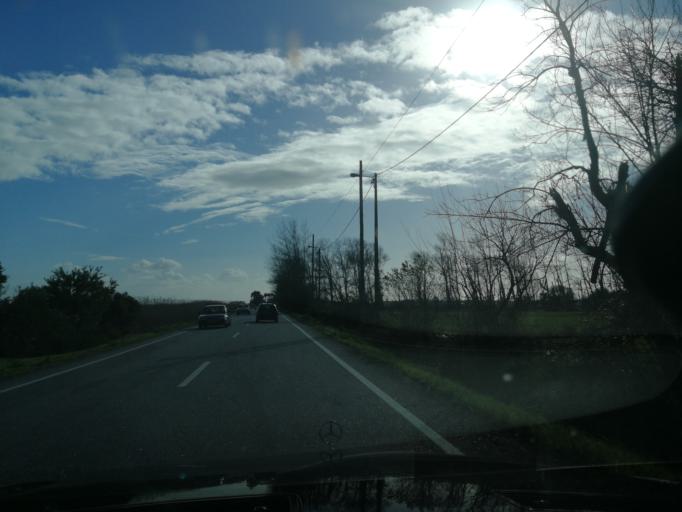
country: PT
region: Aveiro
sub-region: Estarreja
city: Pardilho
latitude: 40.8120
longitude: -8.6712
